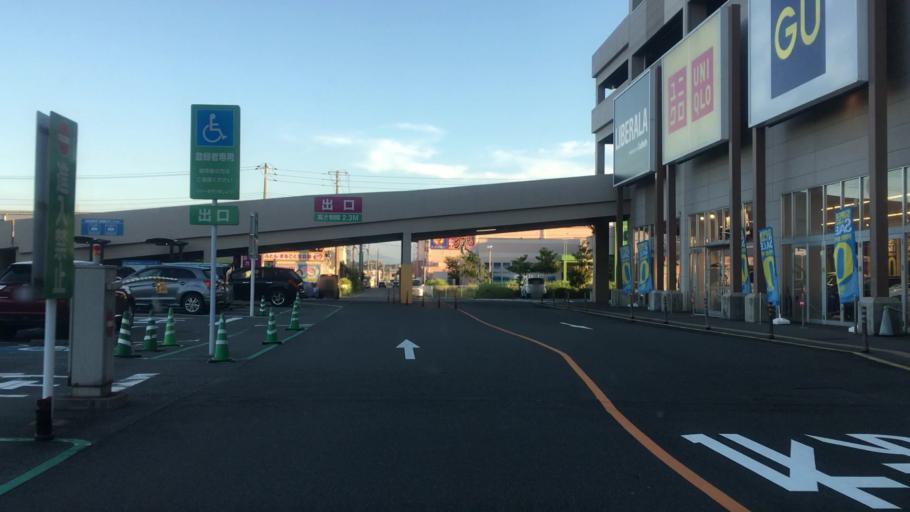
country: JP
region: Tottori
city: Tottori
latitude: 35.5232
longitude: 134.2015
